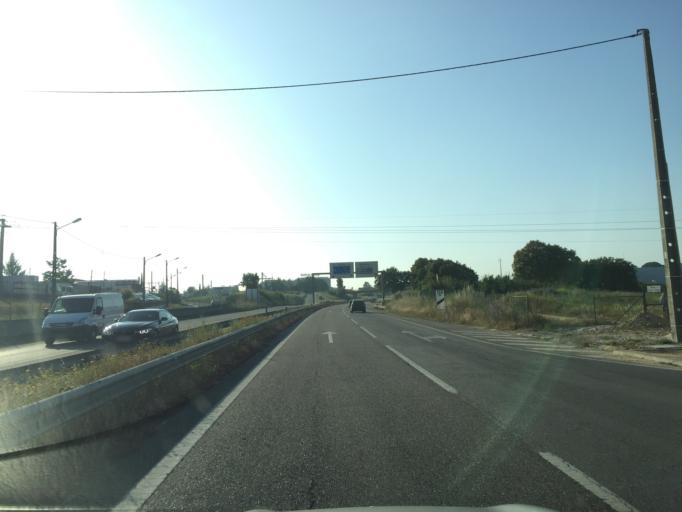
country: PT
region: Santarem
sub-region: Santarem
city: Santarem
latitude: 39.2570
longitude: -8.7011
